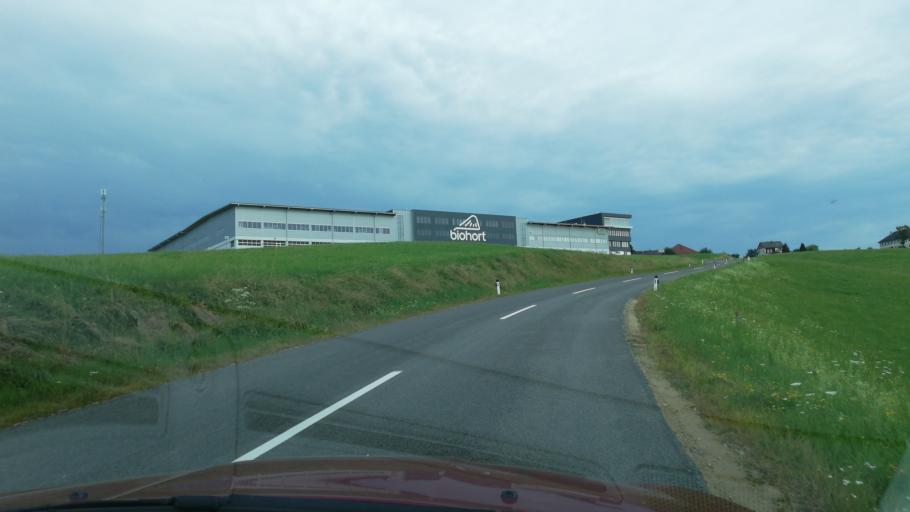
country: AT
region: Upper Austria
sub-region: Politischer Bezirk Rohrbach
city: Kleinzell im Muehlkreis
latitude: 48.4849
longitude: 14.0145
